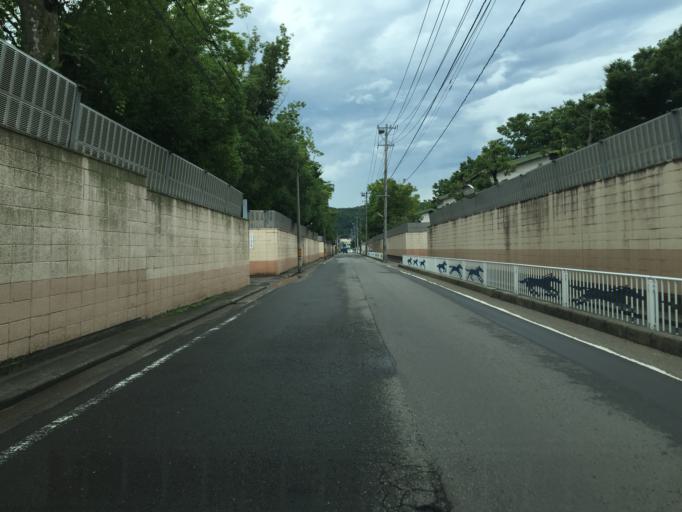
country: JP
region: Fukushima
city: Fukushima-shi
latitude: 37.7681
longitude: 140.4837
